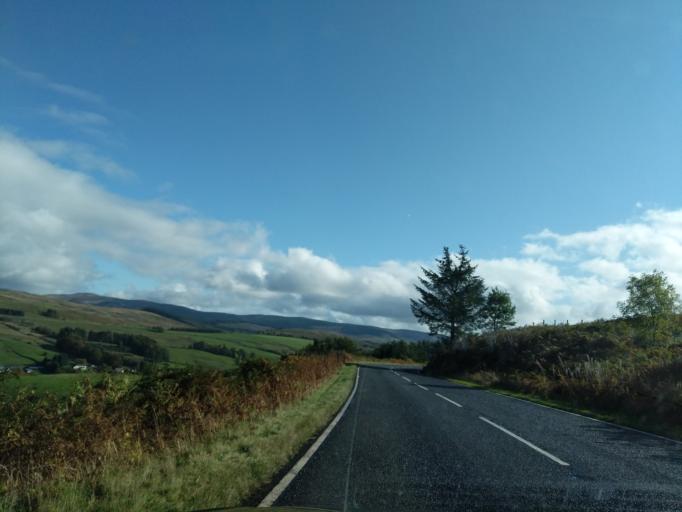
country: GB
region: Scotland
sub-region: Dumfries and Galloway
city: Moffat
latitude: 55.3588
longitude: -3.4740
